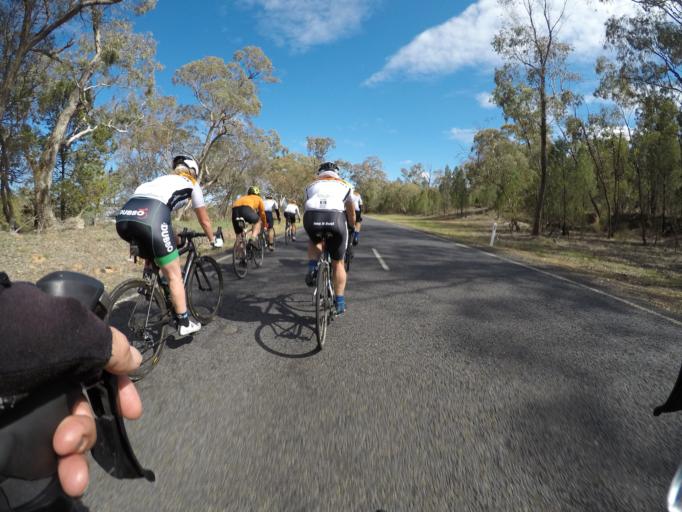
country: AU
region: New South Wales
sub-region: Parkes
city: Peak Hill
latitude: -32.7262
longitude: 148.5620
